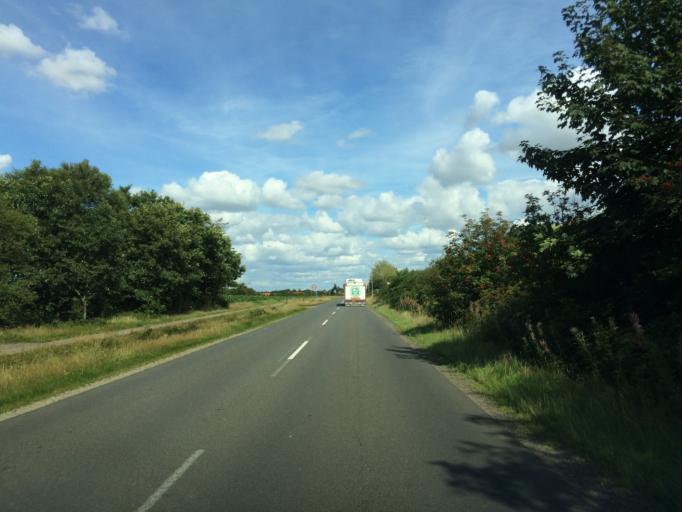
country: DK
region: Central Jutland
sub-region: Ringkobing-Skjern Kommune
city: Skjern
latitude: 55.9440
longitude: 8.4717
